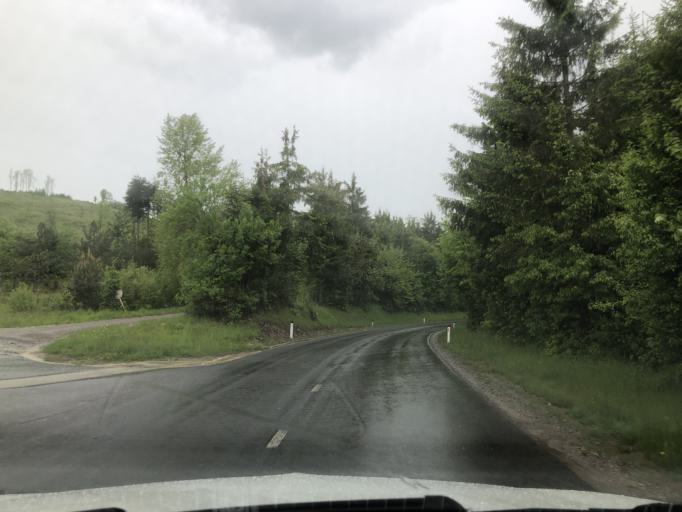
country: SI
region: Postojna
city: Postojna
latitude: 45.7947
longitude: 14.2377
